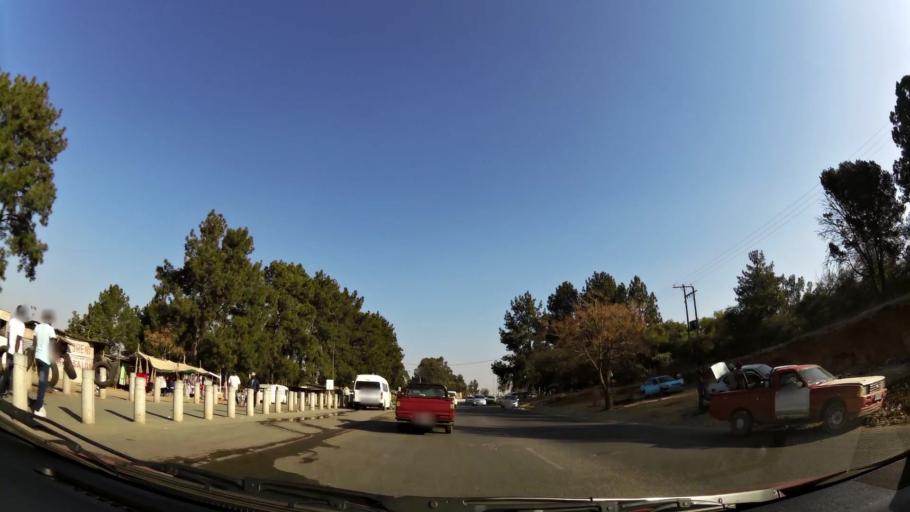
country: ZA
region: Gauteng
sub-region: West Rand District Municipality
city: Muldersdriseloop
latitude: -26.0550
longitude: 27.9043
